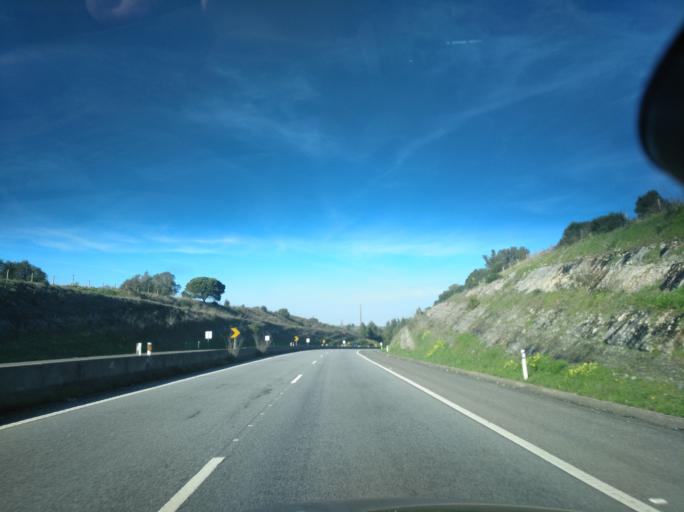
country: PT
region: Lisbon
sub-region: Sintra
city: Pero Pinheiro
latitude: 38.8513
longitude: -9.3496
